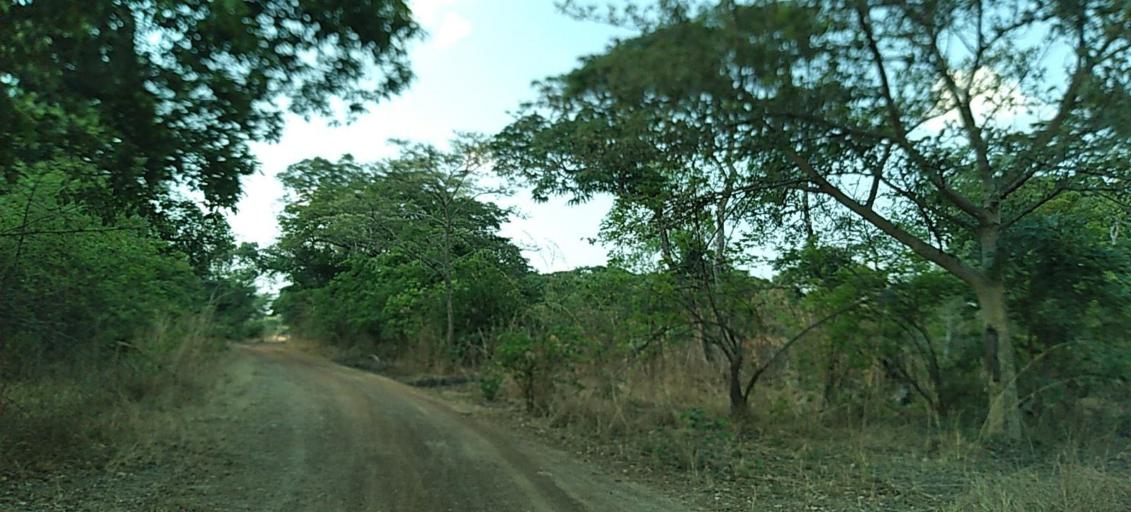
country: ZM
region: Copperbelt
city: Mpongwe
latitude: -13.4637
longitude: 28.0688
